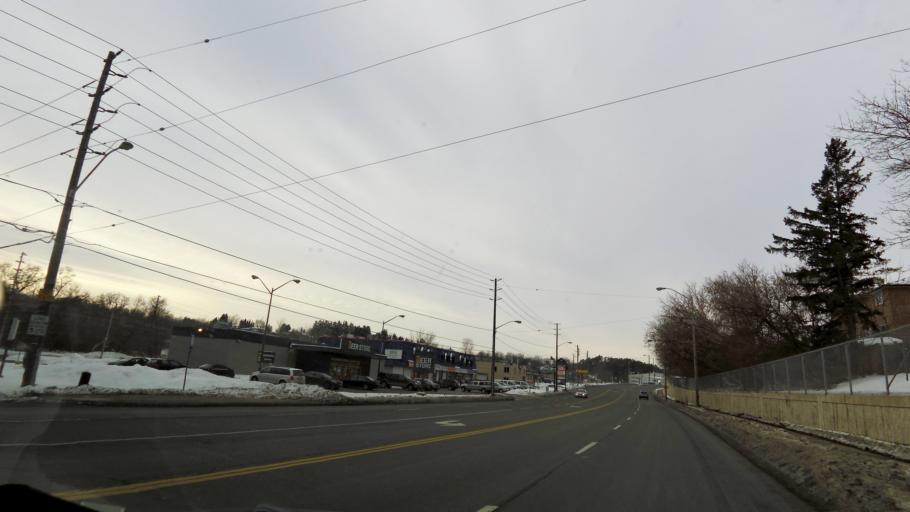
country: CA
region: Ontario
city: Vaughan
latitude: 43.7793
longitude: -79.5866
